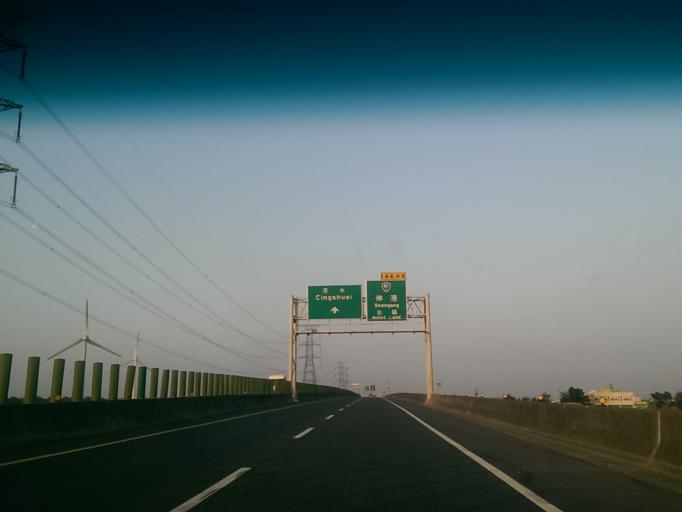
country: TW
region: Taiwan
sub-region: Changhua
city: Chang-hua
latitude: 24.1496
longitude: 120.4530
